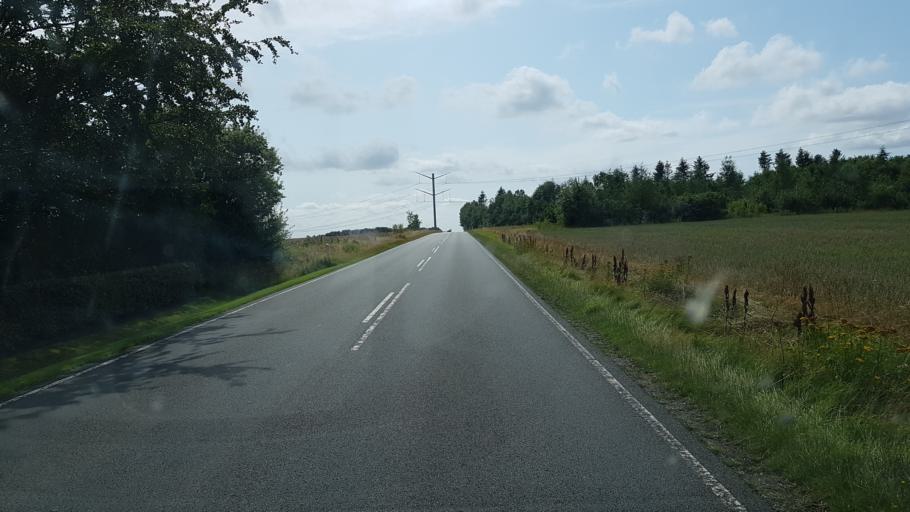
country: DK
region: South Denmark
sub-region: Vejen Kommune
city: Vejen
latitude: 55.5825
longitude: 9.1599
